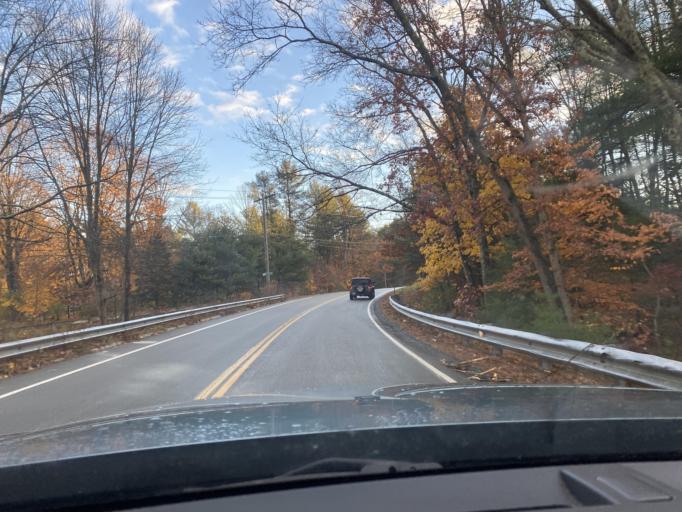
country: US
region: Massachusetts
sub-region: Norfolk County
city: Dover
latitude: 42.2498
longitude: -71.2660
